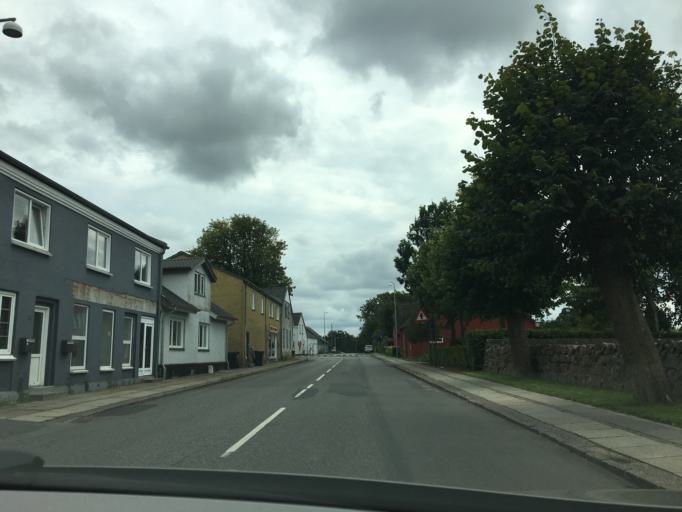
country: DK
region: South Denmark
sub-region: Vejle Kommune
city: Jelling
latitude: 55.7020
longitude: 9.3817
